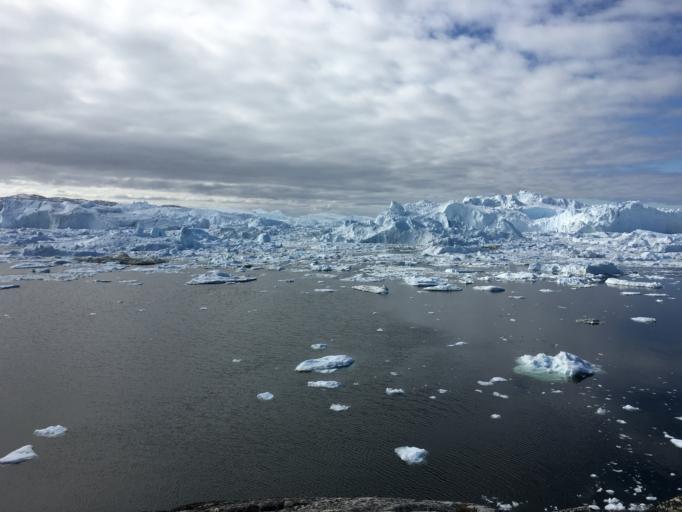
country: GL
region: Qaasuitsup
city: Ilulissat
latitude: 69.1999
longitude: -51.1254
